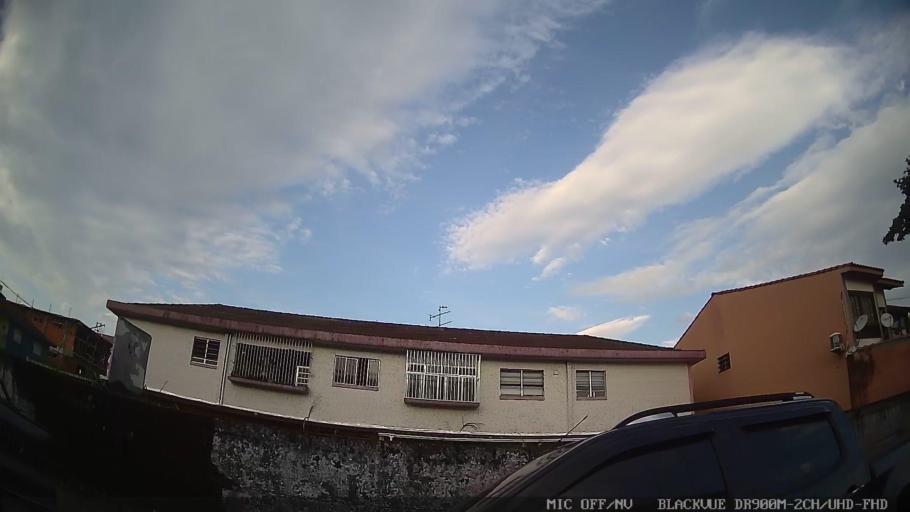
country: BR
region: Sao Paulo
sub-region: Cubatao
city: Cubatao
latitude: -23.8976
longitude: -46.4240
